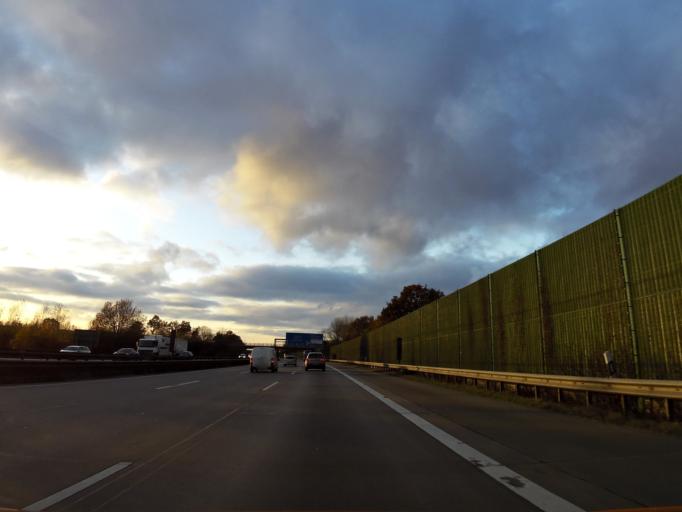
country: DE
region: Lower Saxony
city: Riede
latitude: 53.0390
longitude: 8.9033
